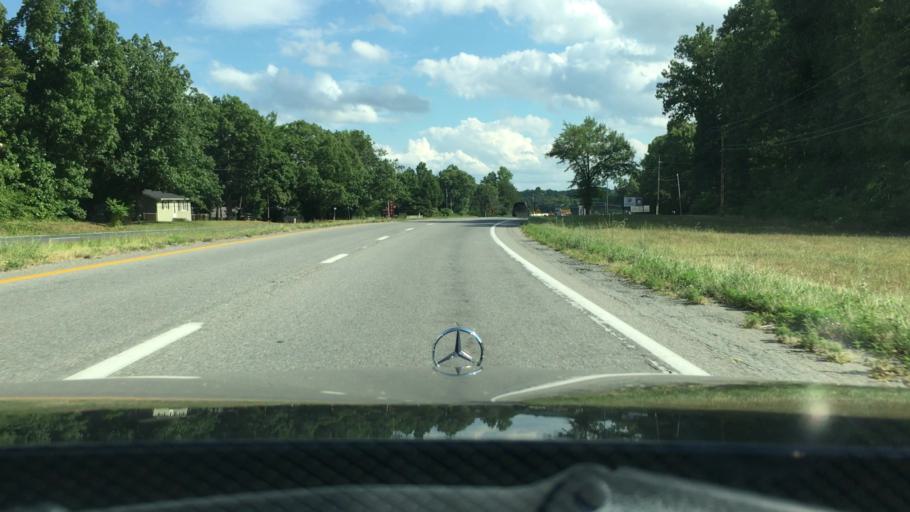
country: US
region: Virginia
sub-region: Campbell County
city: Rustburg
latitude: 37.2355
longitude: -79.1857
